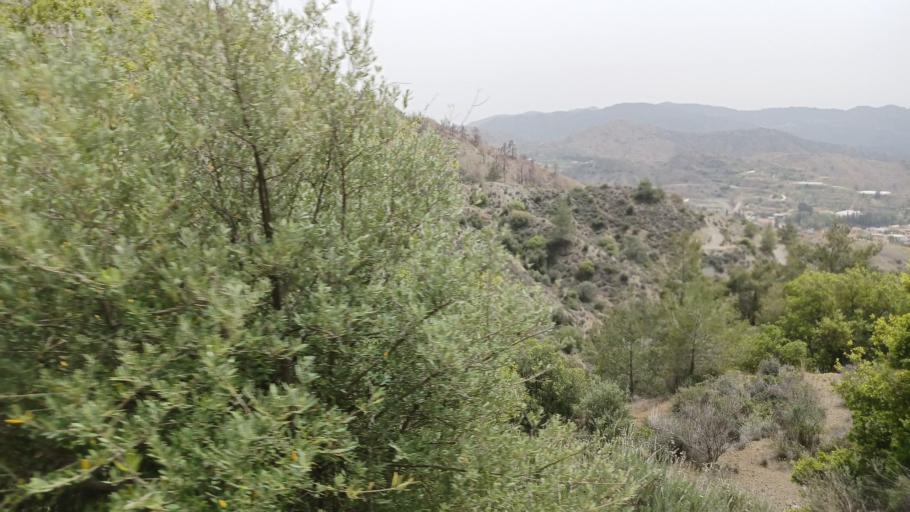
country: CY
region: Limassol
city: Parekklisha
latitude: 34.8516
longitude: 33.1073
